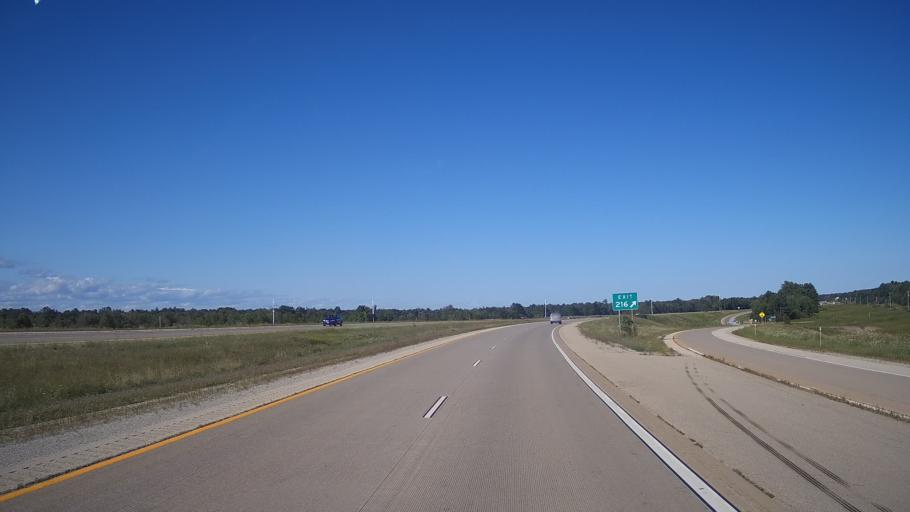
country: US
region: Wisconsin
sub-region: Marinette County
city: Peshtigo
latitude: 45.0570
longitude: -87.7171
